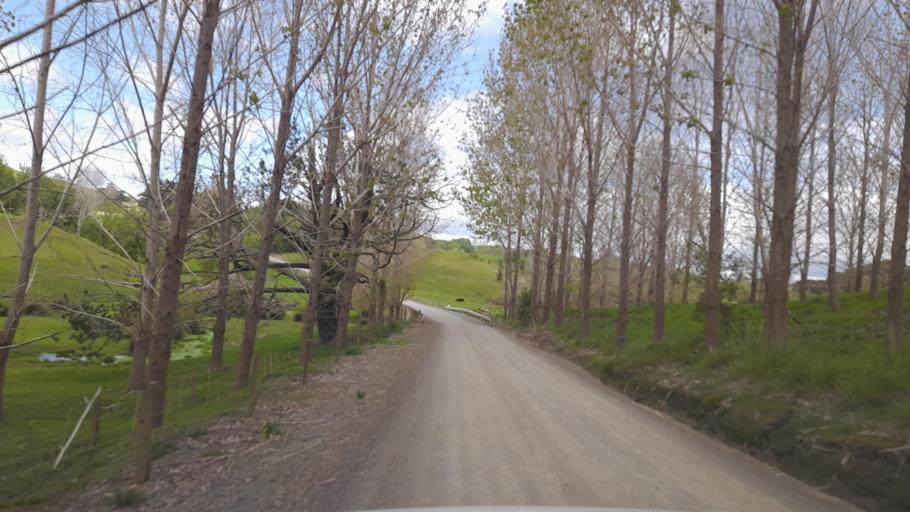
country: NZ
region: Auckland
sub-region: Auckland
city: Wellsford
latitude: -36.1752
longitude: 174.3158
